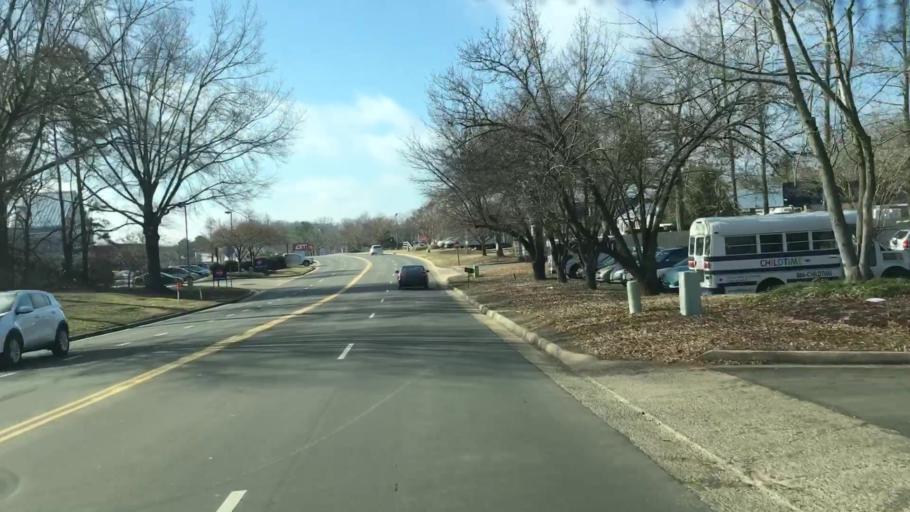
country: US
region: Virginia
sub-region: Chesterfield County
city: Bon Air
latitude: 37.5086
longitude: -77.6164
